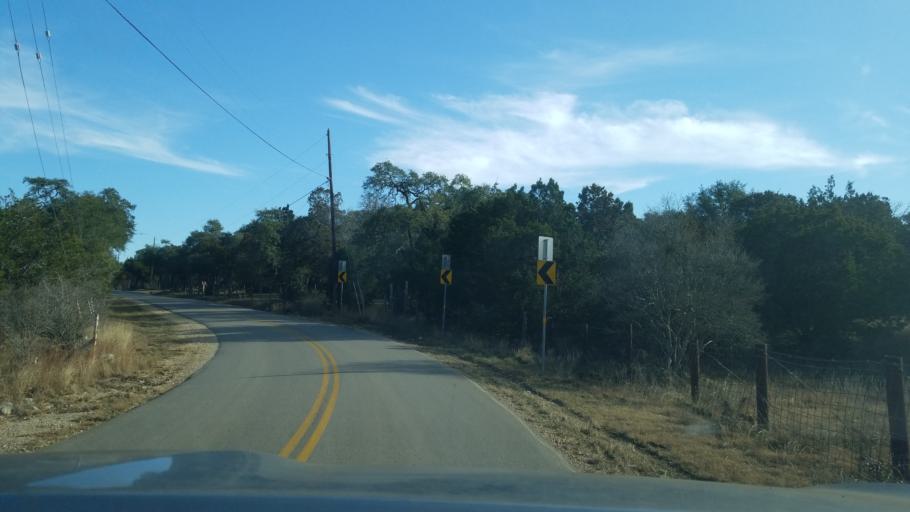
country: US
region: Texas
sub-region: Comal County
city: Canyon Lake
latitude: 29.7815
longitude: -98.2814
